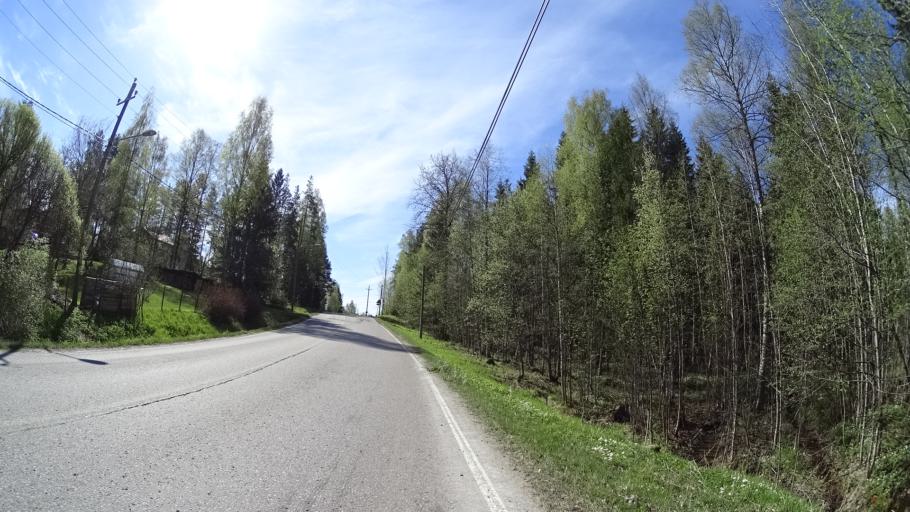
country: FI
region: Uusimaa
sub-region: Helsinki
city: Nurmijaervi
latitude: 60.3871
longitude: 24.8365
